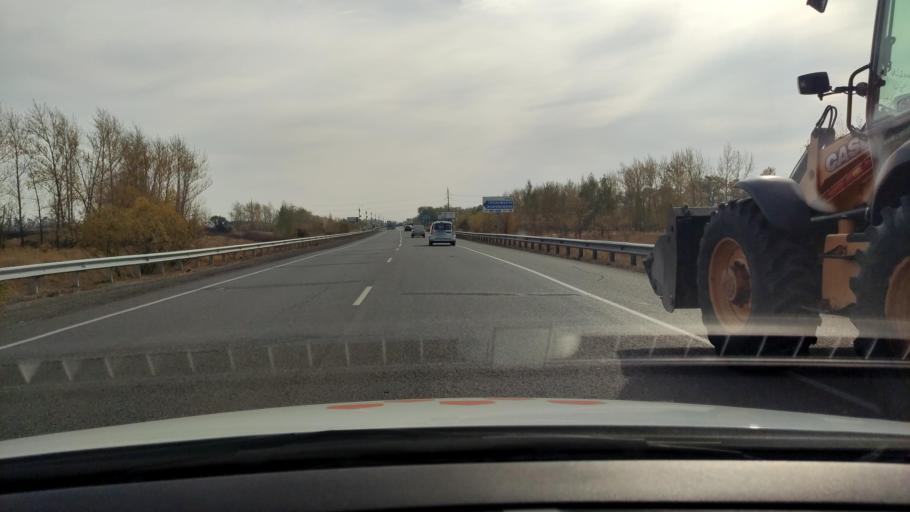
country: RU
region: Voronezj
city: Novaya Usman'
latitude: 51.6960
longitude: 39.4380
